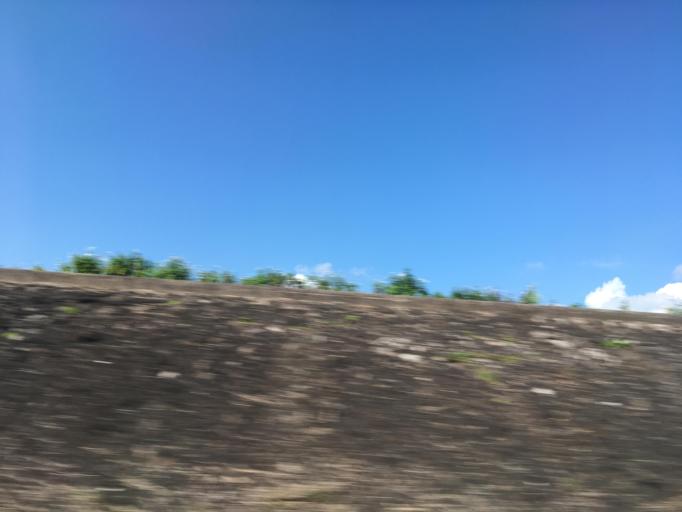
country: TW
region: Taiwan
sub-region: Yilan
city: Yilan
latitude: 24.7570
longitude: 121.7324
